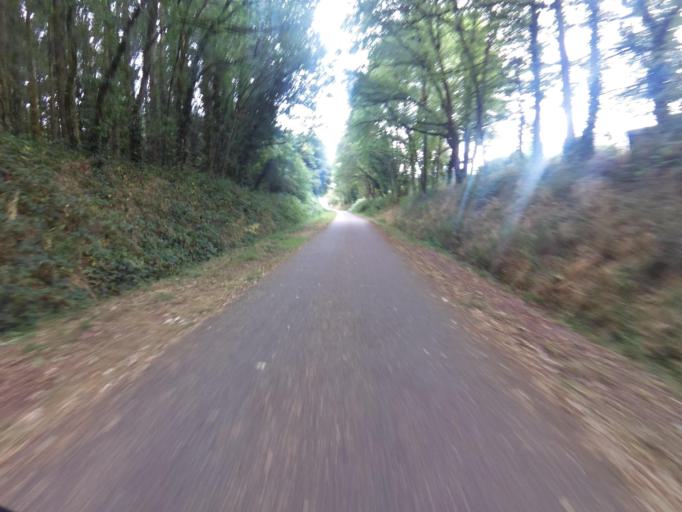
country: FR
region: Brittany
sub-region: Departement du Morbihan
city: Ploermel
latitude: 47.9208
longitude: -2.4252
